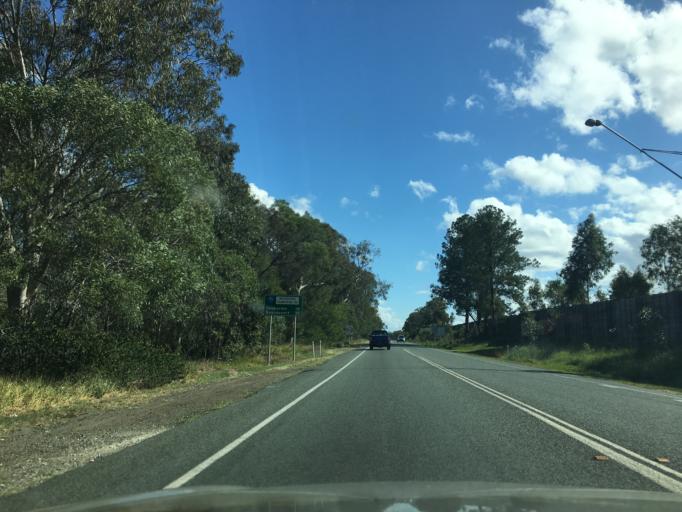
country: AU
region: Queensland
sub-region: Logan
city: Chambers Flat
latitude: -27.7716
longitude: 153.1057
